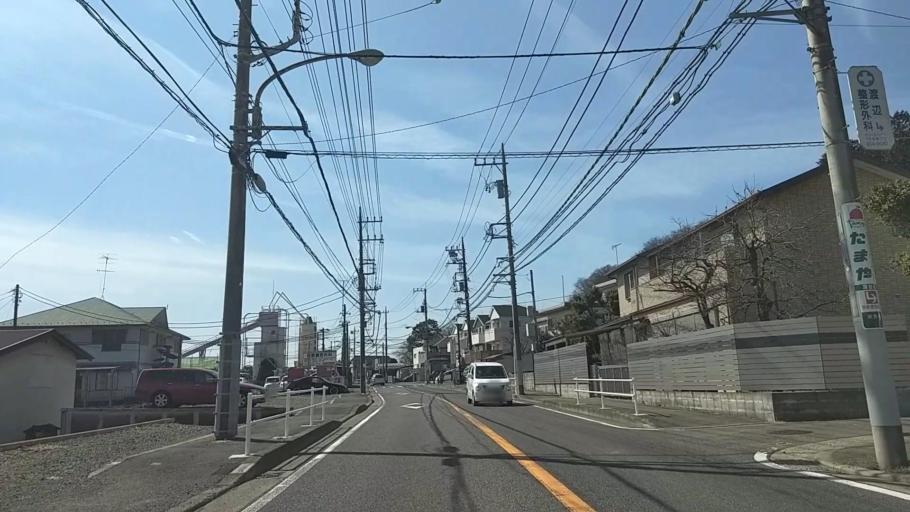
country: JP
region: Kanagawa
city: Fujisawa
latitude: 35.3823
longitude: 139.4974
